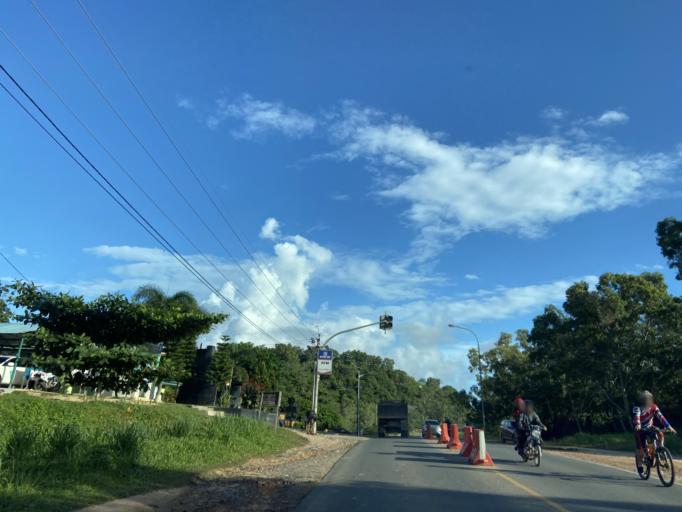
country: SG
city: Singapore
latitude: 1.0034
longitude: 104.0254
